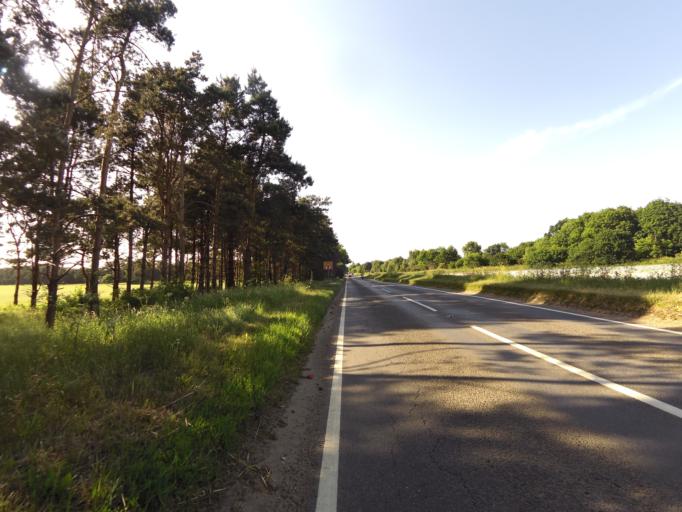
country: GB
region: England
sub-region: Suffolk
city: Woodbridge
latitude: 52.0908
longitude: 1.3536
